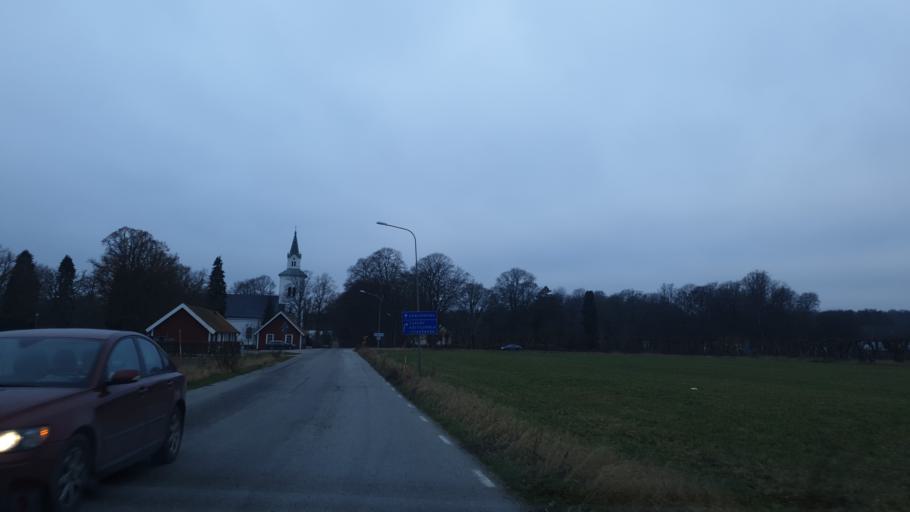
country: SE
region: Blekinge
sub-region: Karlskrona Kommun
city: Rodeby
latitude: 56.2168
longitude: 15.6794
